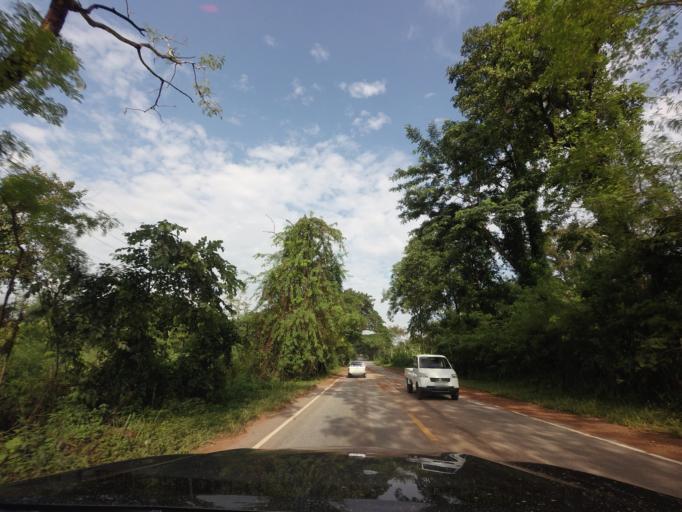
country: TH
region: Nong Khai
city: Pho Tak
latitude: 17.7850
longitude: 102.3717
